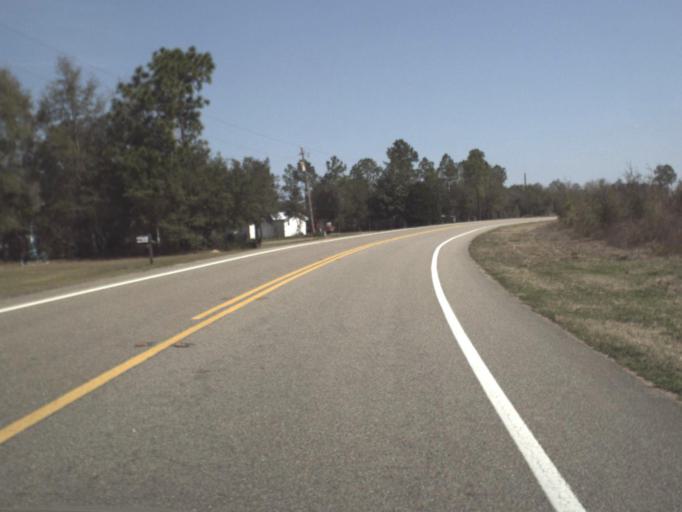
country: US
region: Florida
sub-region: Liberty County
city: Bristol
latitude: 30.5056
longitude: -84.8758
